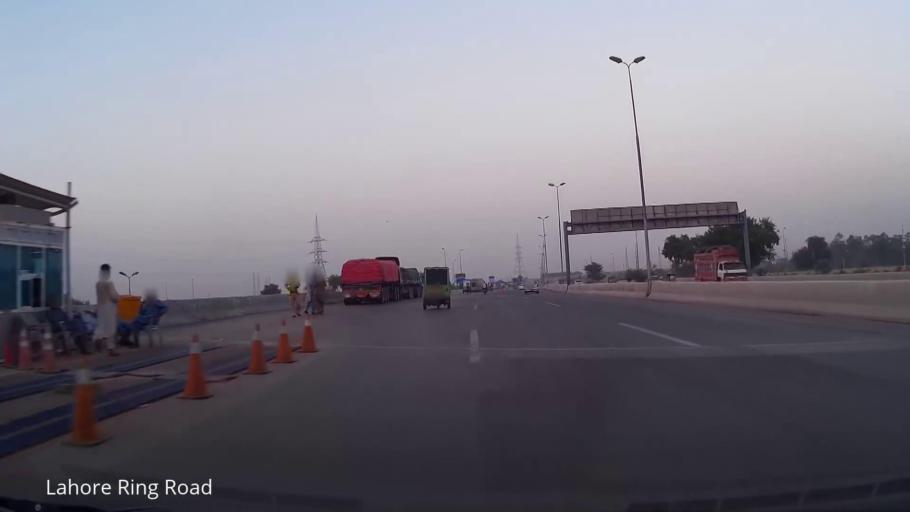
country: PK
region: Punjab
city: Lahore
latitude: 31.6063
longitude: 74.2999
